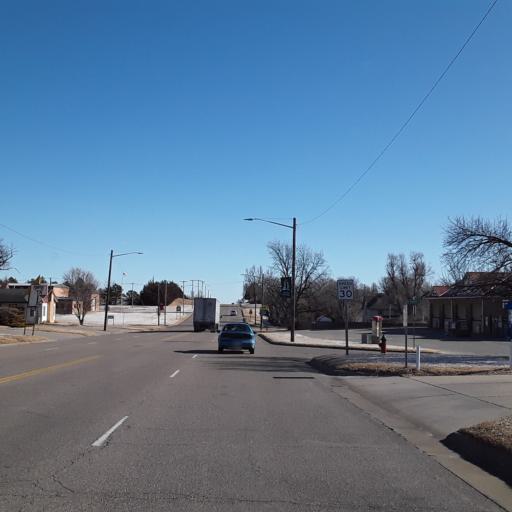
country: US
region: Kansas
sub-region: Pawnee County
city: Larned
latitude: 38.1881
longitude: -99.0976
